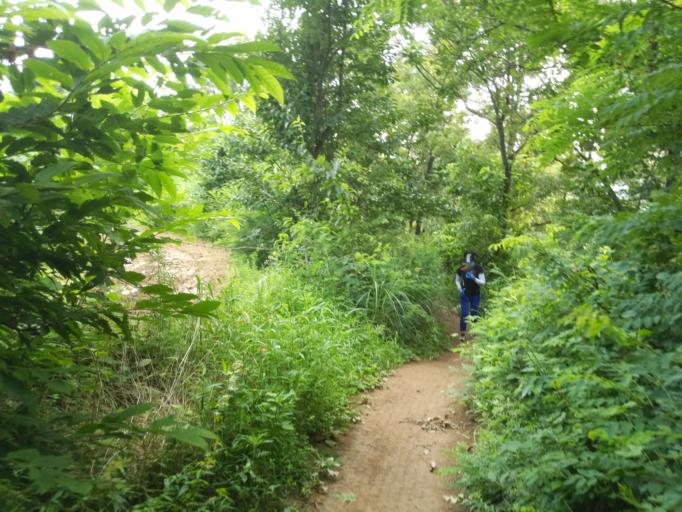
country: KR
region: Daegu
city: Hwawon
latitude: 35.8008
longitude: 128.5270
